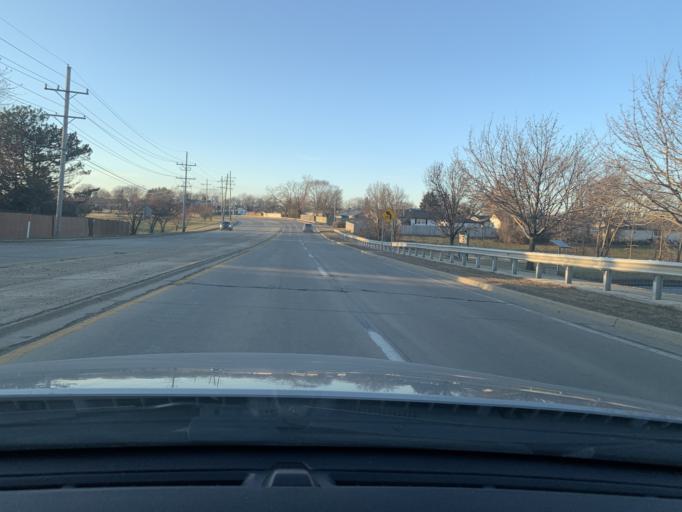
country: US
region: Illinois
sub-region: DuPage County
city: Itasca
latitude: 41.9983
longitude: -88.0366
